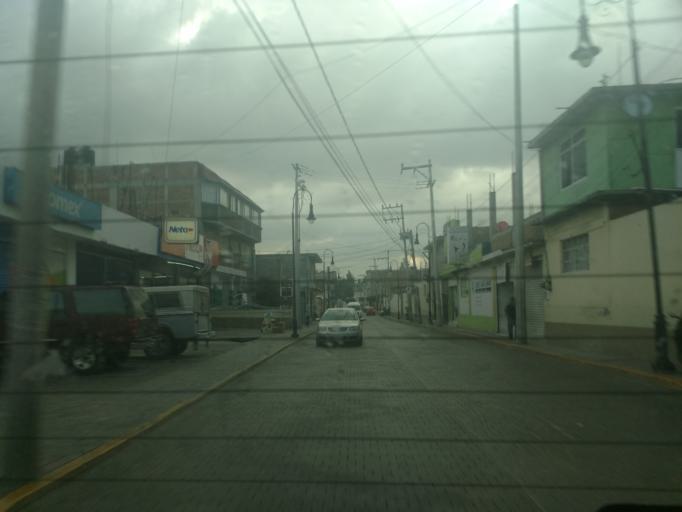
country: MX
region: Morelos
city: Coyotepec
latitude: 19.7758
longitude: -99.2102
